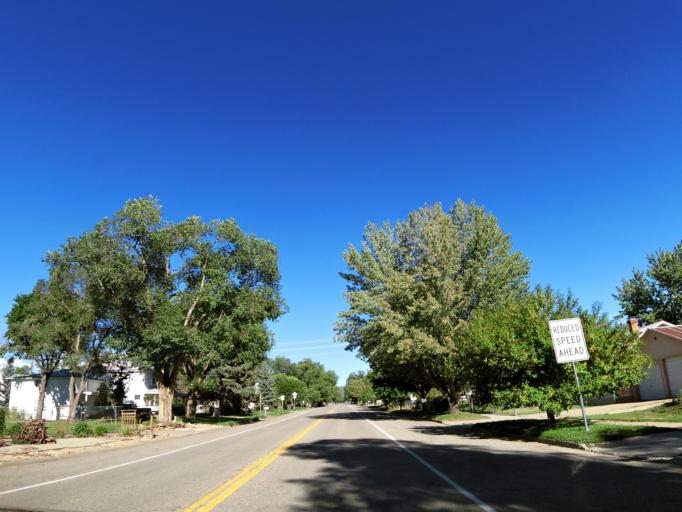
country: US
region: Colorado
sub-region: Montezuma County
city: Mancos
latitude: 37.3450
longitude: -108.2997
